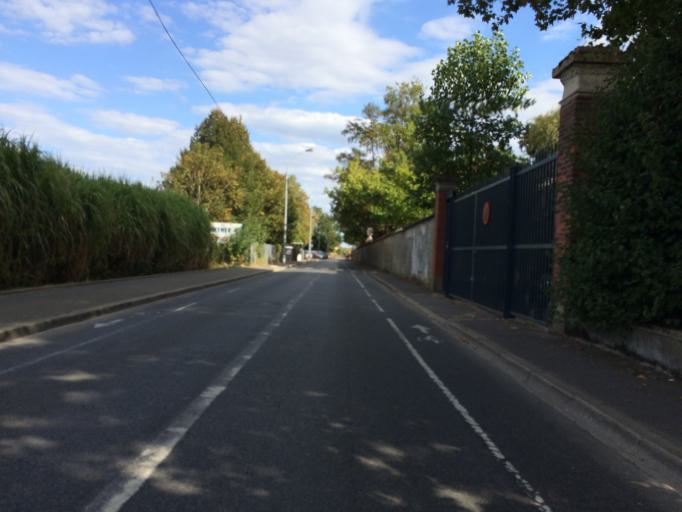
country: FR
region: Ile-de-France
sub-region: Departement de l'Essonne
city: Chilly-Mazarin
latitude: 48.7095
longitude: 2.3159
